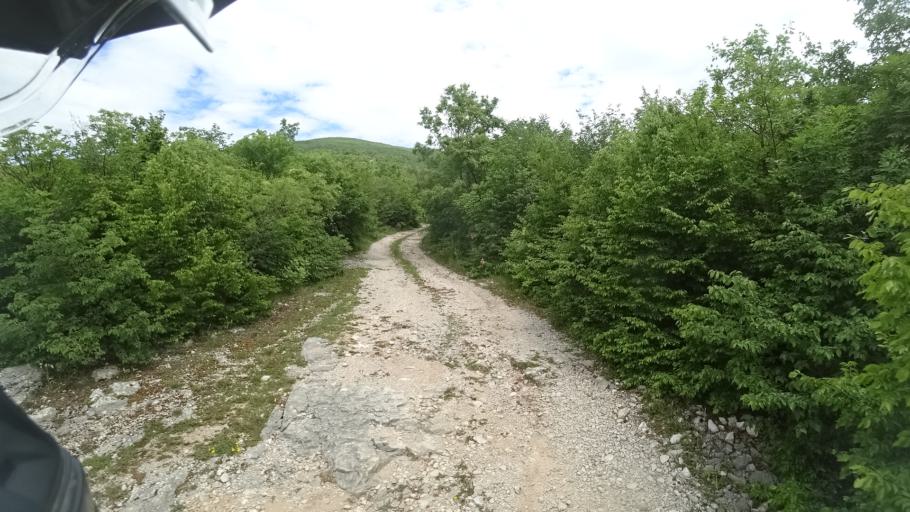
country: HR
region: Splitsko-Dalmatinska
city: Hrvace
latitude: 43.8944
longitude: 16.5446
